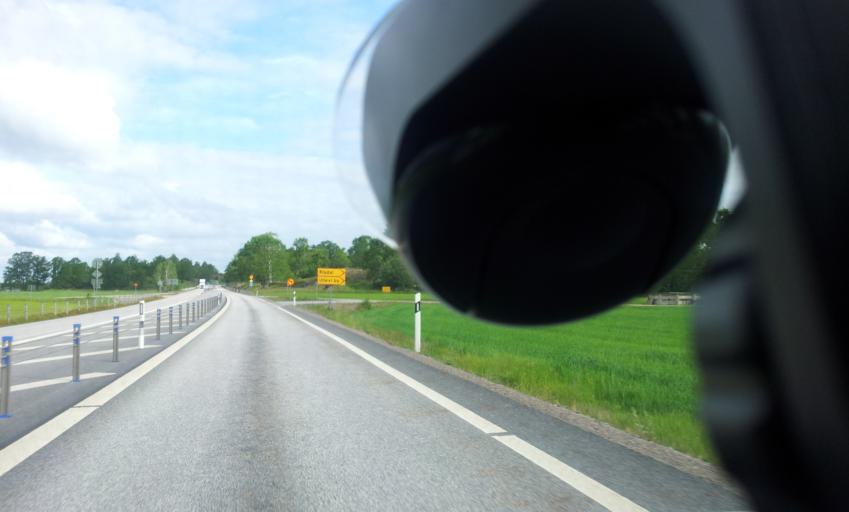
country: SE
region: Kalmar
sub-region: Vasterviks Kommun
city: Gamleby
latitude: 57.8781
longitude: 16.3992
